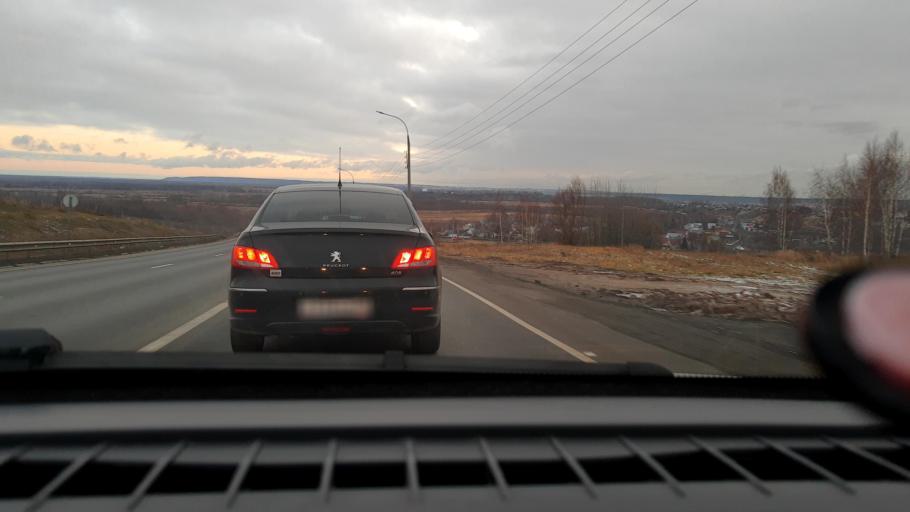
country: RU
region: Nizjnij Novgorod
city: Afonino
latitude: 56.2428
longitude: 44.1016
